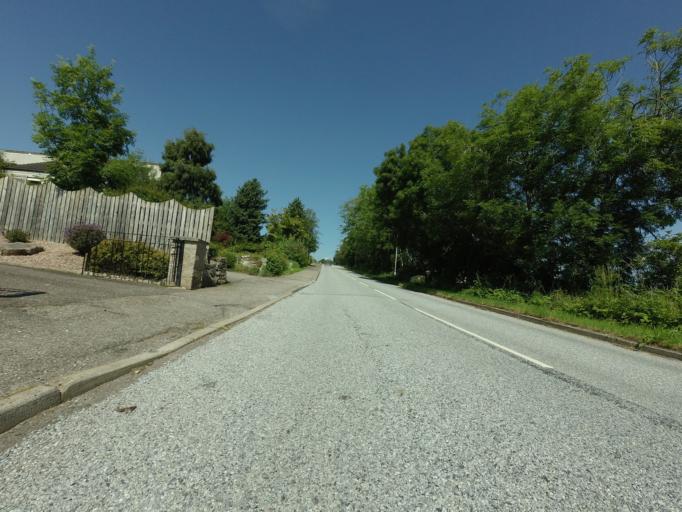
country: GB
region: Scotland
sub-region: Highland
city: Dingwall
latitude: 57.6079
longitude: -4.4217
